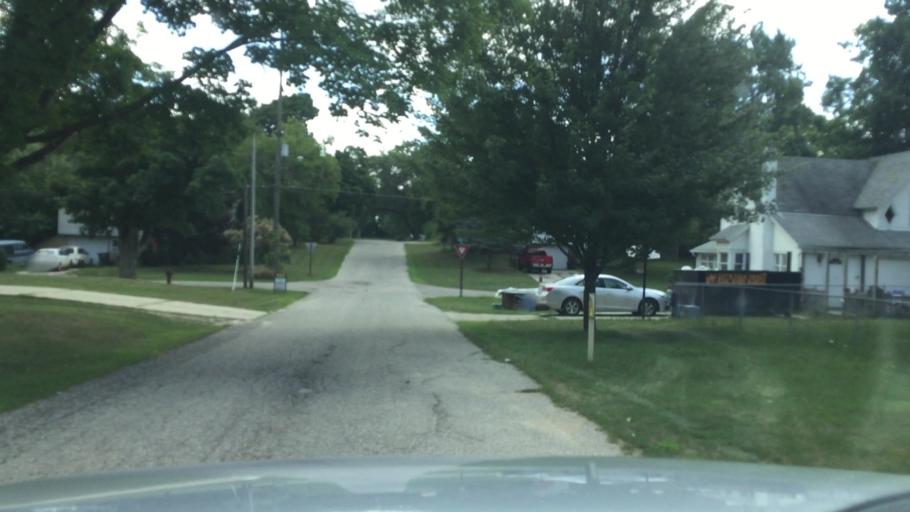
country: US
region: Michigan
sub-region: Ionia County
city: Belding
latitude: 43.1030
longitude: -85.2365
